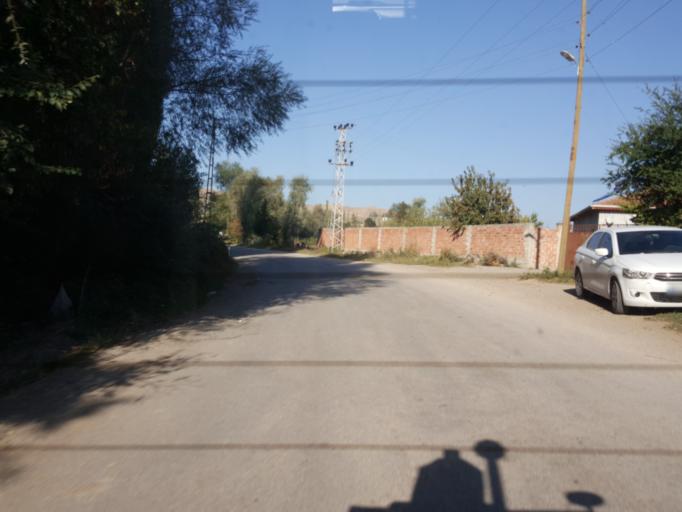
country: TR
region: Amasya
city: Saribugday
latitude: 40.7496
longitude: 35.4563
